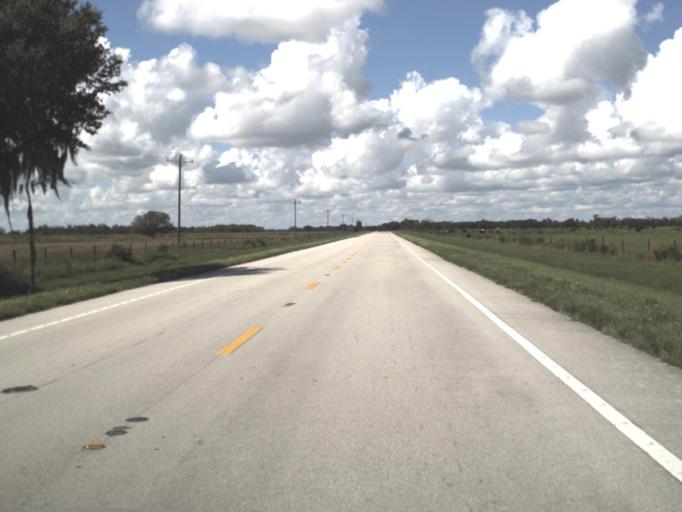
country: US
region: Florida
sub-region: DeSoto County
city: Arcadia
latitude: 27.2431
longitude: -81.9464
